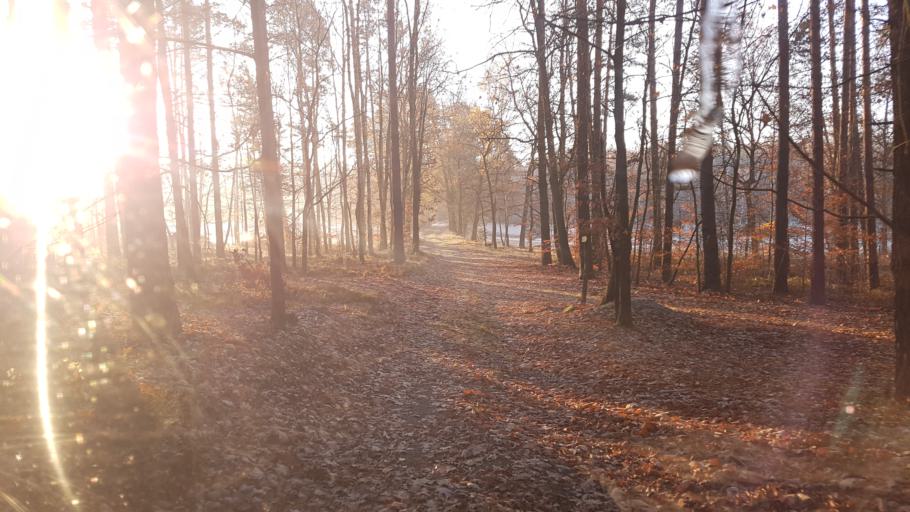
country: DE
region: Brandenburg
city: Sallgast
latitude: 51.6016
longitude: 13.8350
